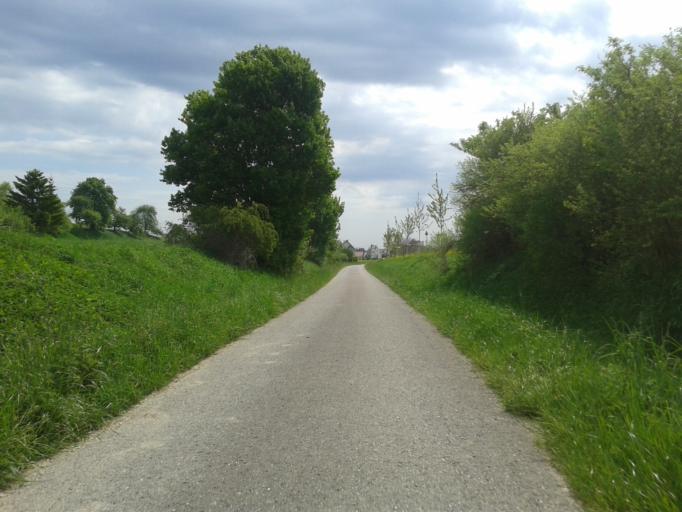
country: DE
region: Baden-Wuerttemberg
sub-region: Tuebingen Region
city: Erbach
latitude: 48.3546
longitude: 9.8873
